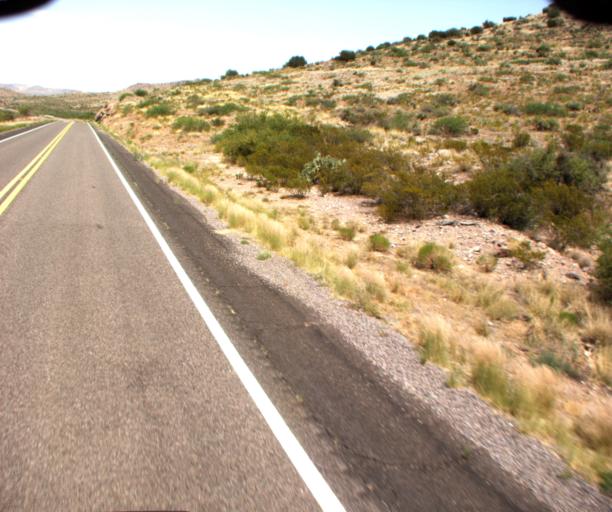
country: US
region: Arizona
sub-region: Greenlee County
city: Clifton
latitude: 32.7569
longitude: -109.3265
